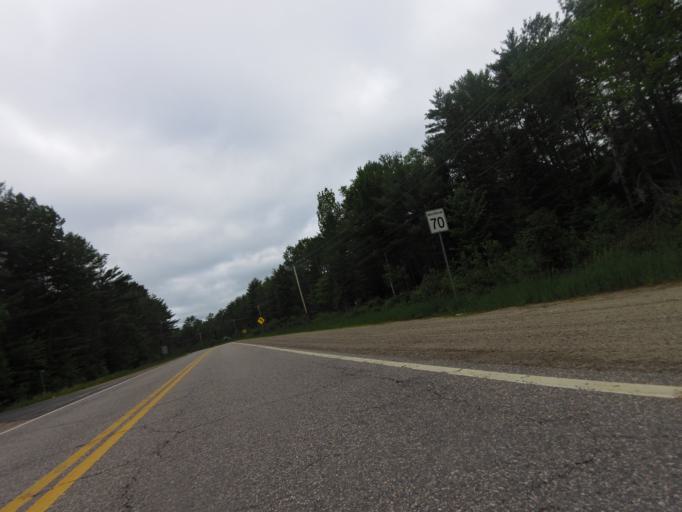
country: CA
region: Quebec
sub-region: Outaouais
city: Shawville
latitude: 45.8588
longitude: -76.4198
